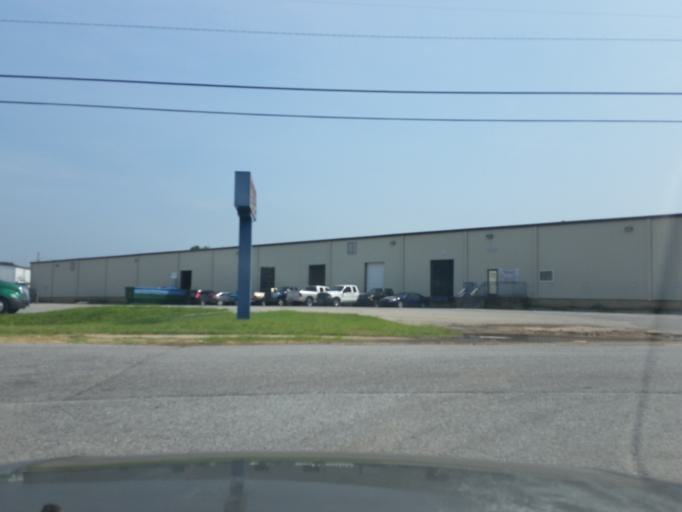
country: US
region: Florida
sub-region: Escambia County
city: Goulding
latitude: 30.4486
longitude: -87.2330
